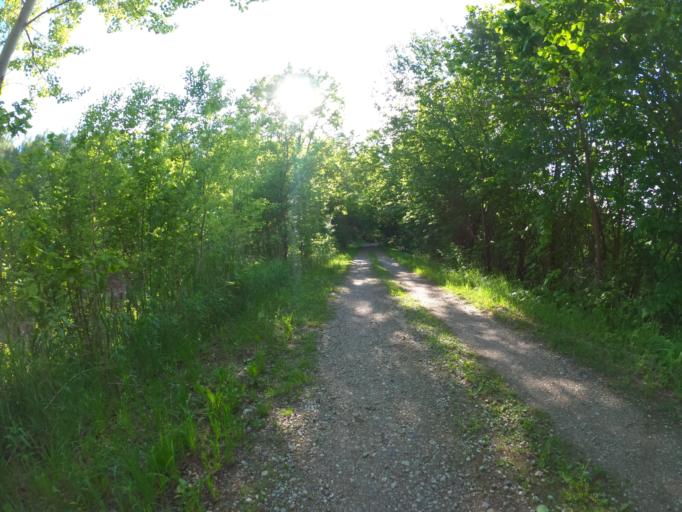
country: PL
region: Warmian-Masurian Voivodeship
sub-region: Powiat lidzbarski
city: Lidzbark Warminski
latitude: 54.1250
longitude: 20.6003
